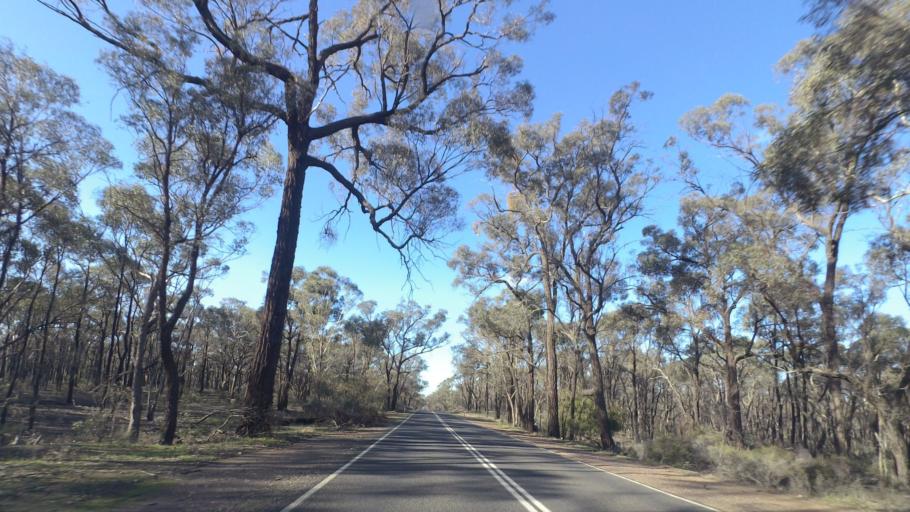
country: AU
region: Victoria
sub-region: Greater Bendigo
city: Epsom
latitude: -36.6650
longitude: 144.4418
